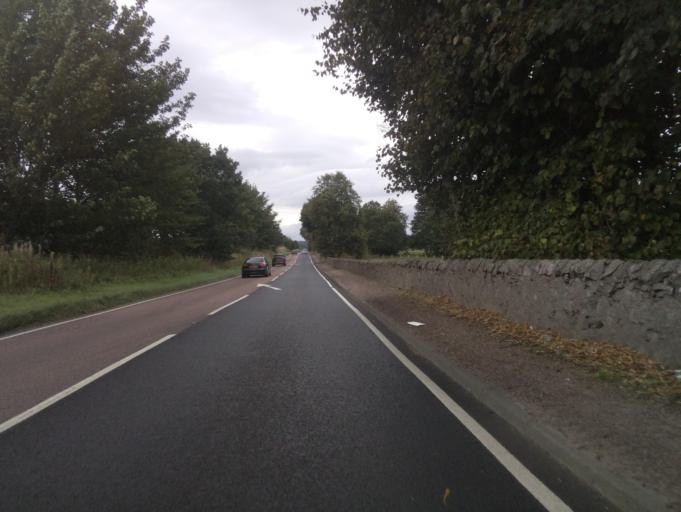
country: GB
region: Scotland
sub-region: Fife
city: Leuchars
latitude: 56.3896
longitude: -2.8999
